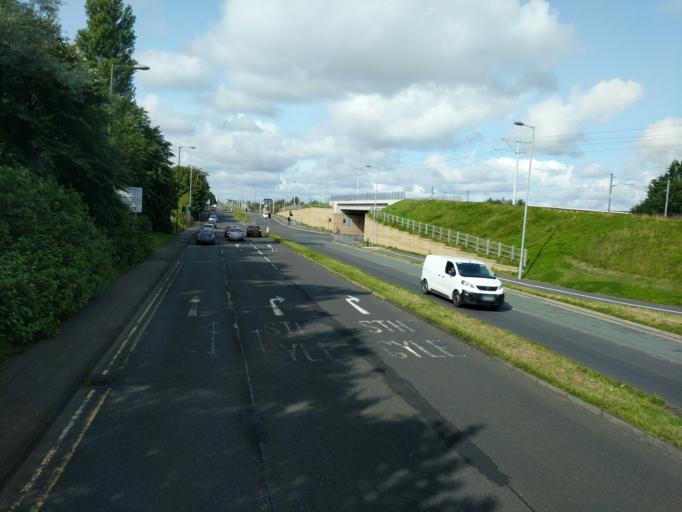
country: GB
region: Scotland
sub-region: Edinburgh
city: Currie
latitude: 55.9291
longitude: -3.2899
